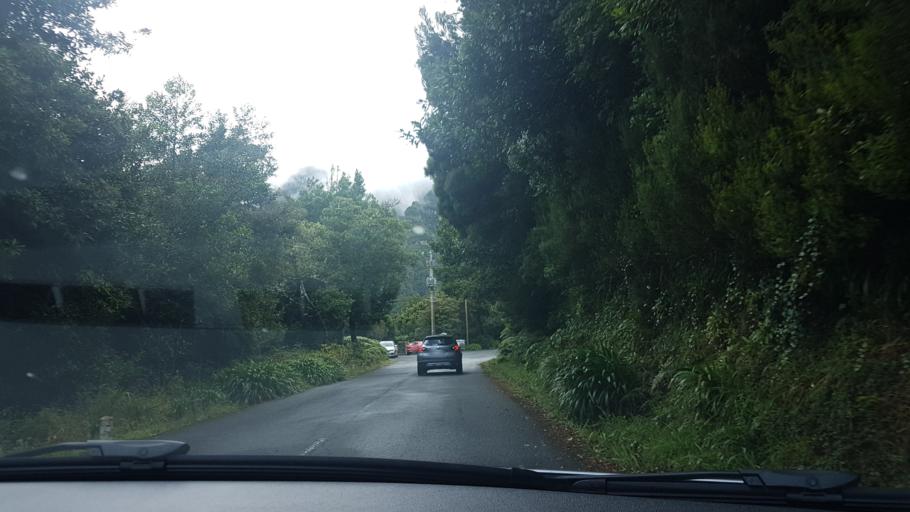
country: PT
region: Madeira
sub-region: Sao Vicente
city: Sao Vicente
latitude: 32.7618
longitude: -17.0167
